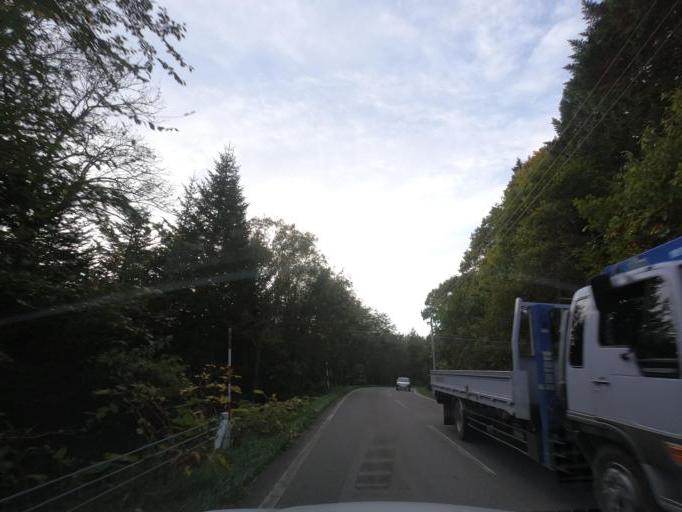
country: JP
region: Hokkaido
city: Obihiro
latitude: 42.5433
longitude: 143.4143
